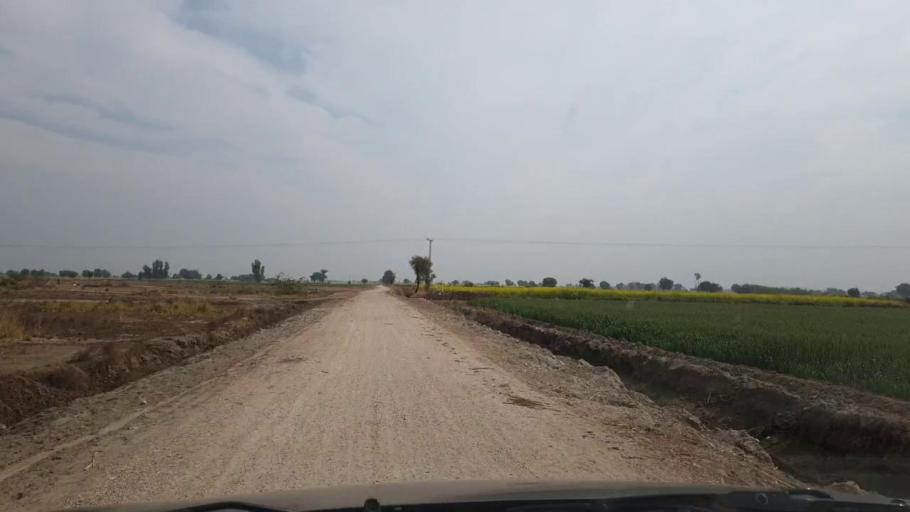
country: PK
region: Sindh
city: Sinjhoro
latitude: 26.0649
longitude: 68.8460
